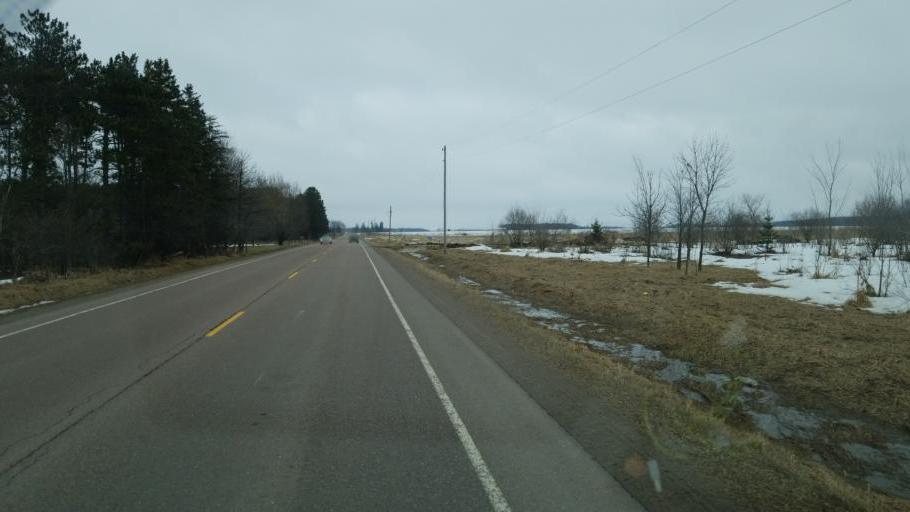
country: US
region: Wisconsin
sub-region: Clark County
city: Loyal
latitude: 44.6543
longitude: -90.4288
